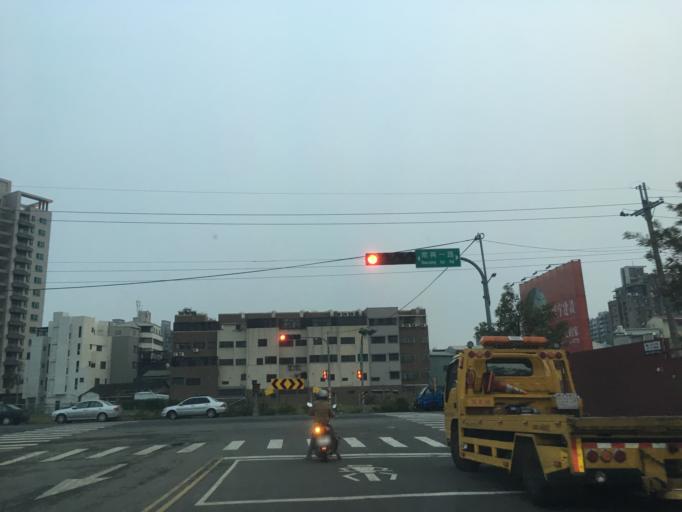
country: TW
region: Taiwan
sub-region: Taichung City
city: Taichung
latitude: 24.1731
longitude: 120.7036
